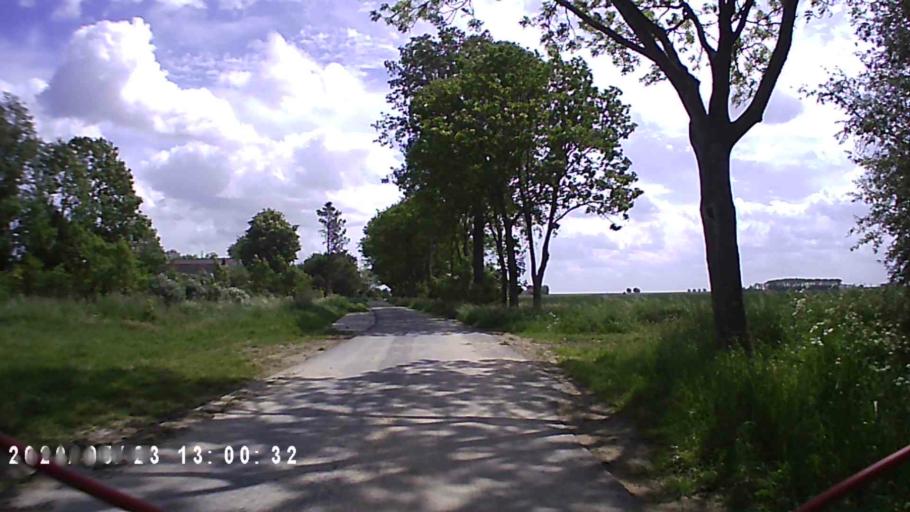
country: NL
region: Groningen
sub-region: Gemeente Delfzijl
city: Delfzijl
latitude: 53.2951
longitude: 7.0576
